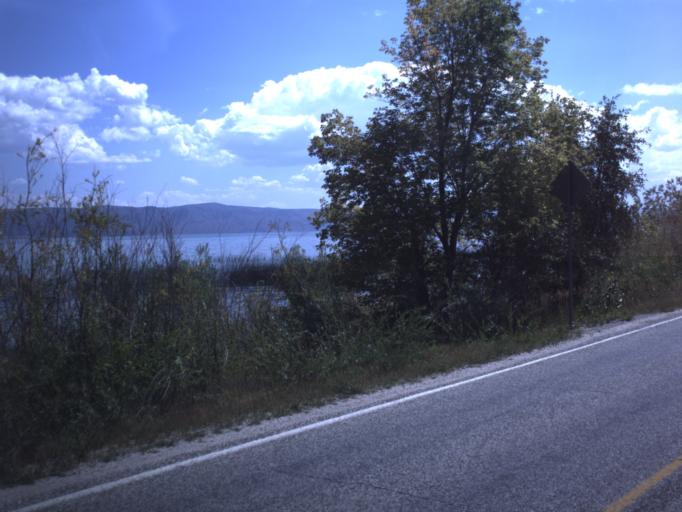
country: US
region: Idaho
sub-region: Bear Lake County
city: Paris
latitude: 41.9761
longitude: -111.4028
